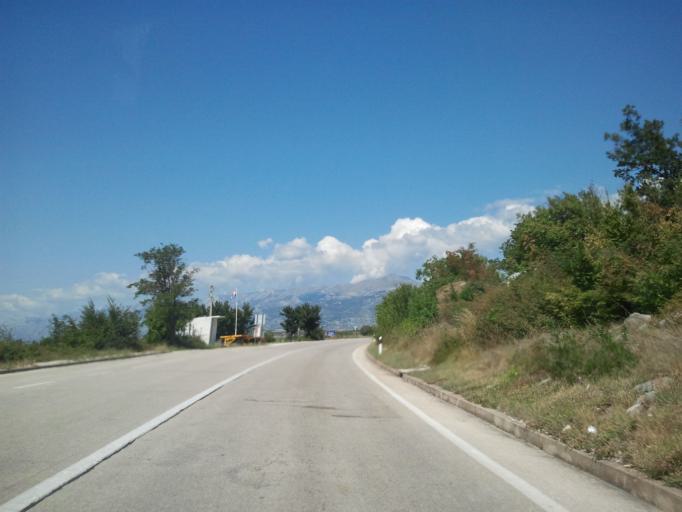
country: HR
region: Zadarska
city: Krusevo
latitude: 44.1763
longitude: 15.6168
